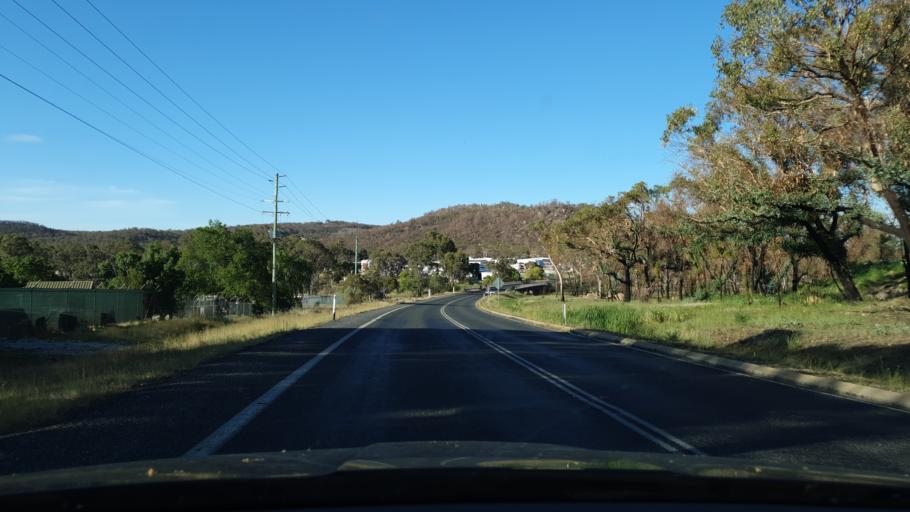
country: AU
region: Queensland
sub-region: Southern Downs
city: Stanthorpe
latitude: -28.6555
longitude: 151.9174
